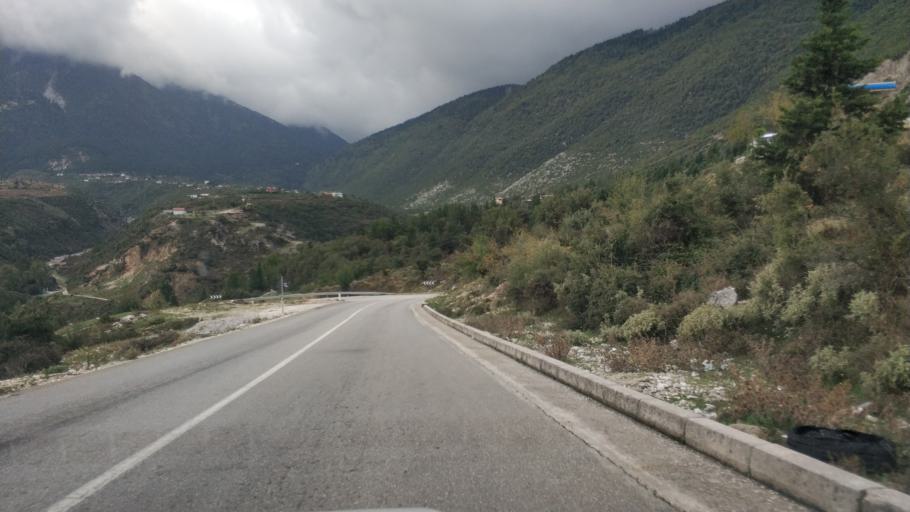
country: AL
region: Vlore
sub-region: Rrethi i Vlores
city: Orikum
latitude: 40.2422
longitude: 19.5506
